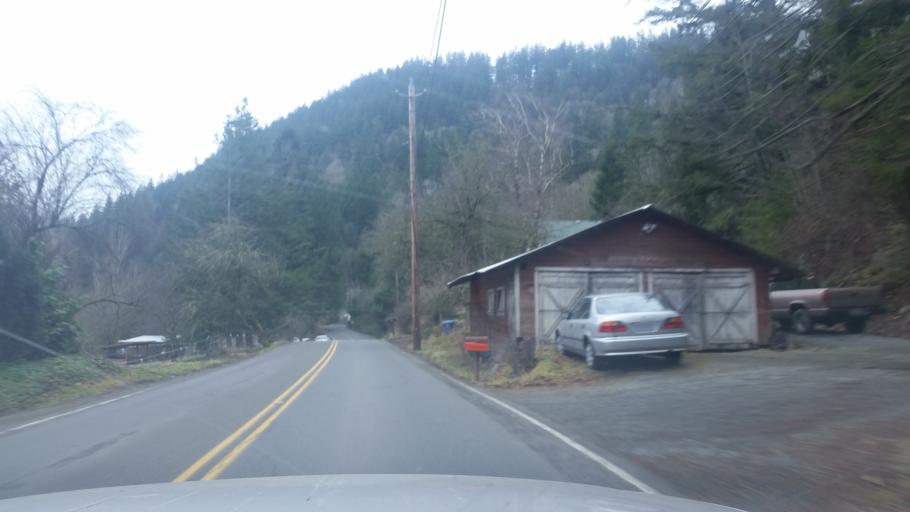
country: US
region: Washington
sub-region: King County
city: Issaquah
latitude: 47.5375
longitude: -121.9692
